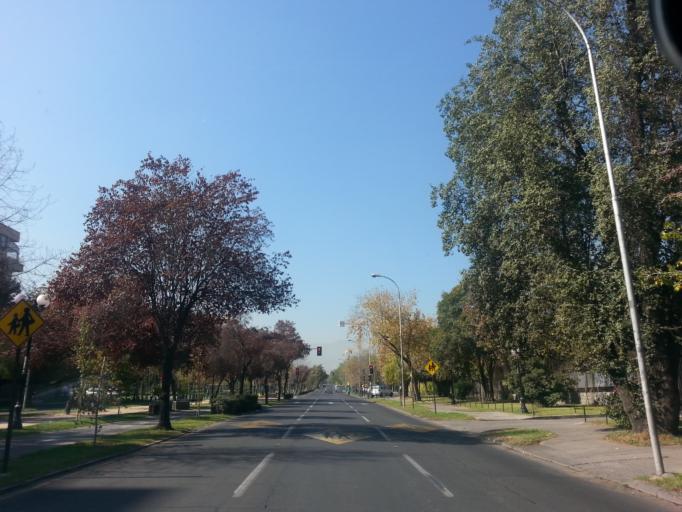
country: CL
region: Santiago Metropolitan
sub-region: Provincia de Santiago
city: Villa Presidente Frei, Nunoa, Santiago, Chile
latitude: -33.4333
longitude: -70.5960
